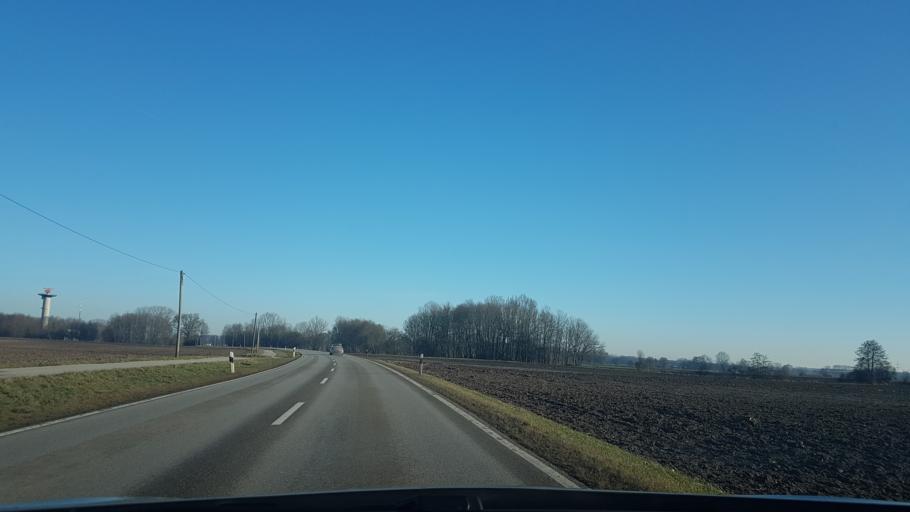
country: DE
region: Bavaria
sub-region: Upper Bavaria
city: Eichenried
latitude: 48.3098
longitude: 11.8045
